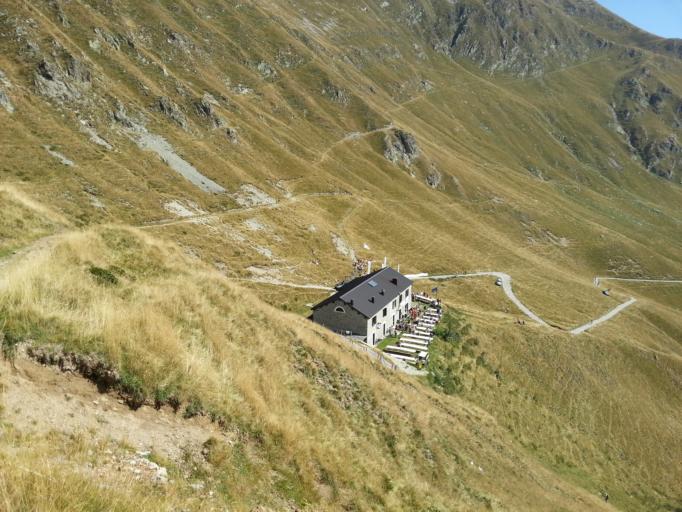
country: CH
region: Grisons
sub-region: Moesa District
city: Roveredo
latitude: 46.1662
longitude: 9.1589
